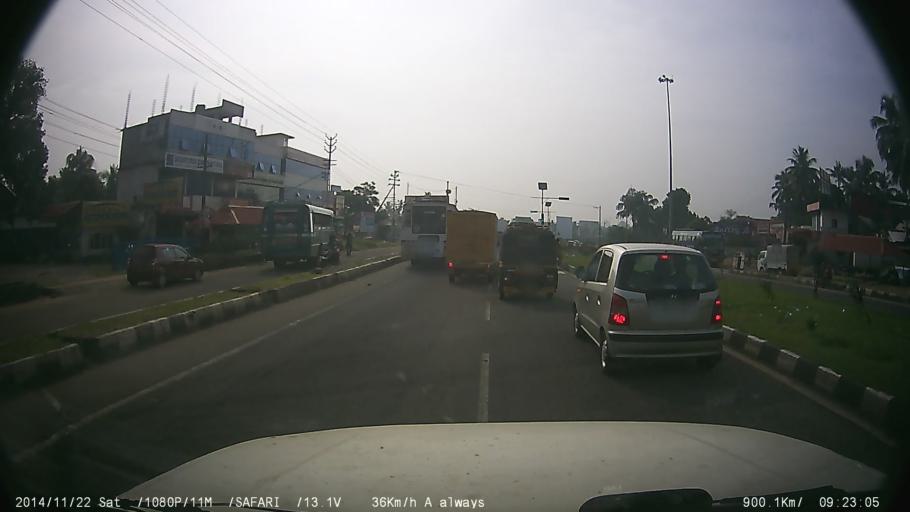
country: IN
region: Kerala
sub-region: Ernakulam
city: Angamali
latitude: 10.2113
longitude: 76.3813
